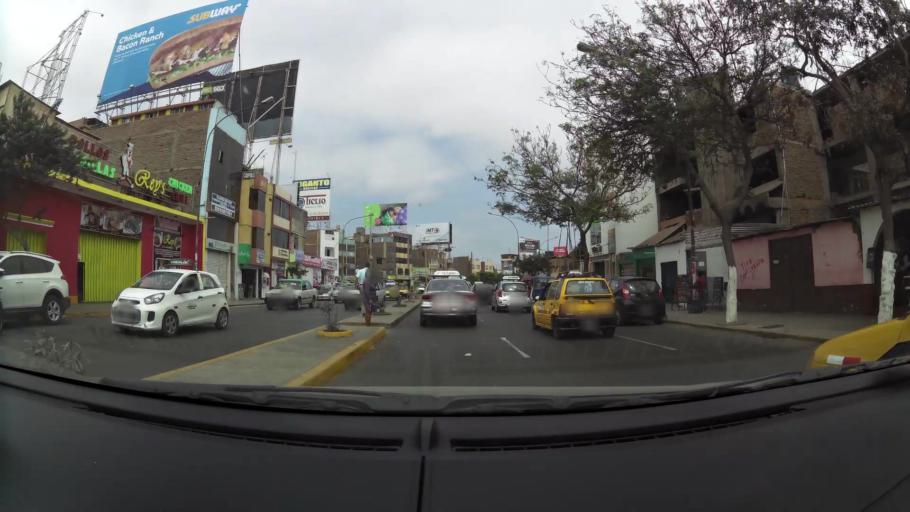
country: PE
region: La Libertad
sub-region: Provincia de Trujillo
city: Trujillo
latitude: -8.1068
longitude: -79.0228
